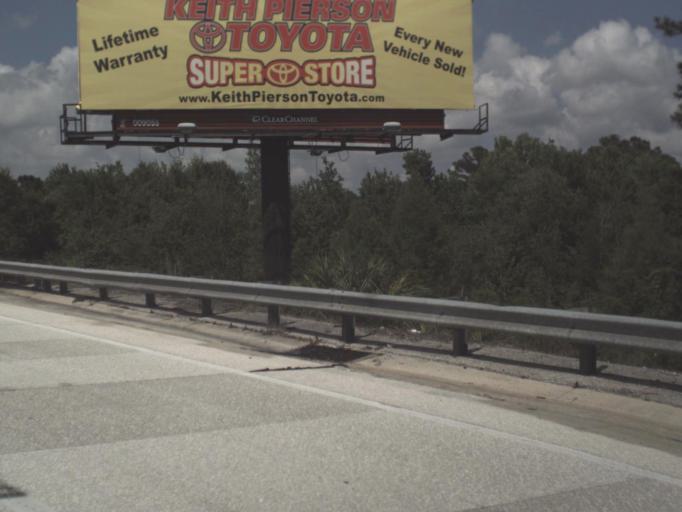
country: US
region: Florida
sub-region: Saint Johns County
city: Fruit Cove
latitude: 30.1821
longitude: -81.5584
